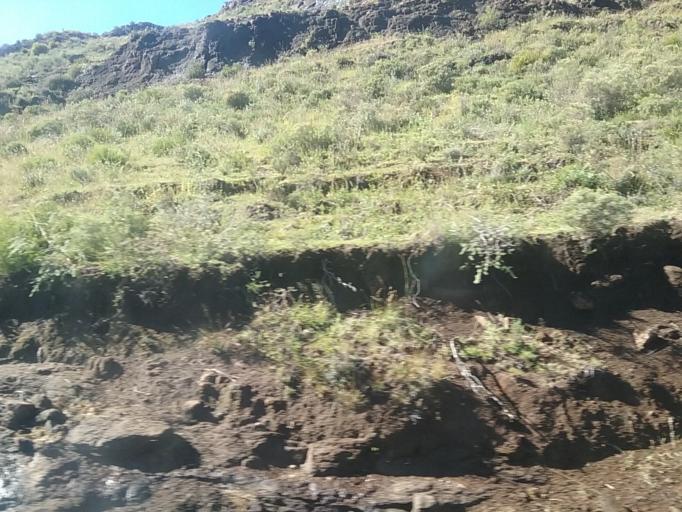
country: LS
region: Berea
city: Teyateyaneng
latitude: -29.2364
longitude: 27.9132
